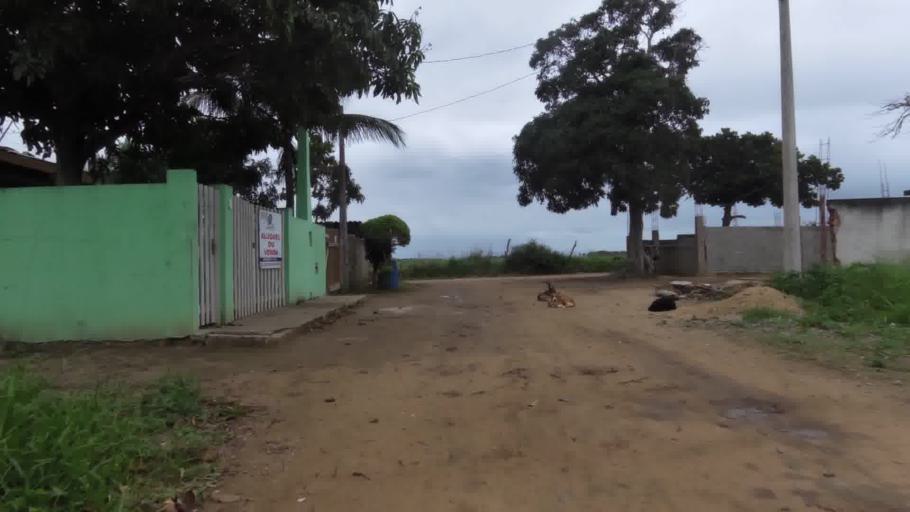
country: BR
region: Espirito Santo
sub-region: Marataizes
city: Marataizes
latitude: -21.0491
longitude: -40.8414
